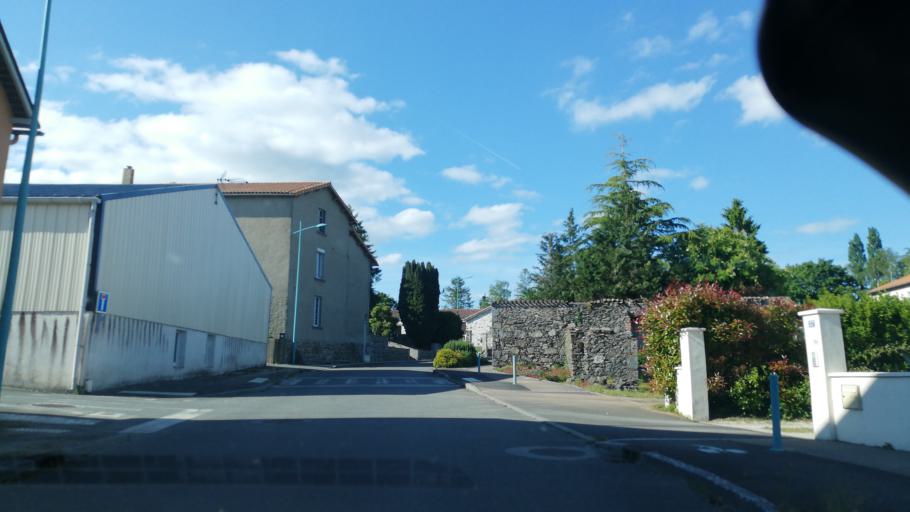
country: FR
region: Poitou-Charentes
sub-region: Departement des Deux-Sevres
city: Moncoutant
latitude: 46.7173
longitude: -0.5876
